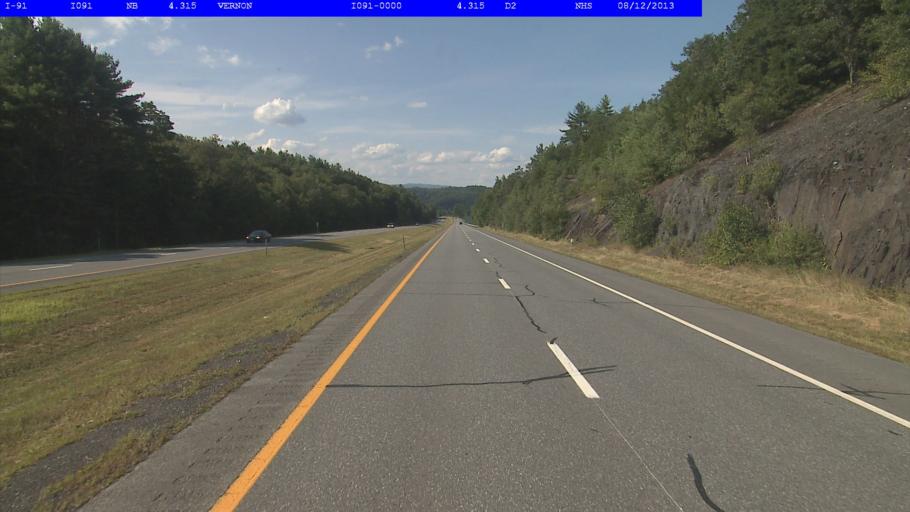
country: US
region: Vermont
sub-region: Windham County
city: Brattleboro
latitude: 42.7920
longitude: -72.5610
